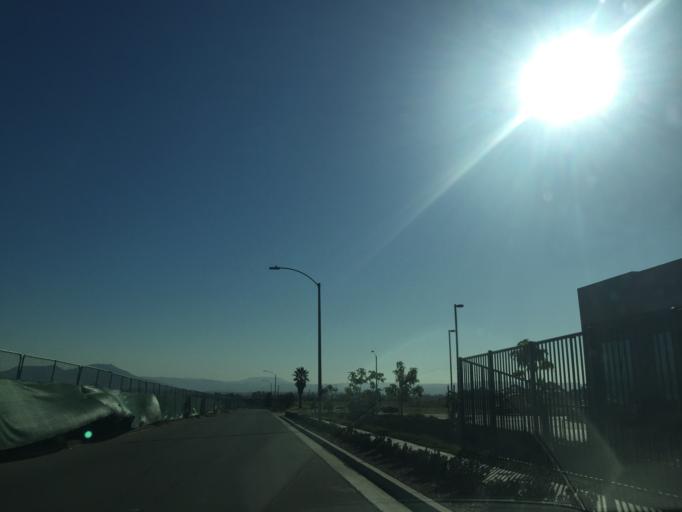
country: MX
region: Baja California
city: Tijuana
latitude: 32.5594
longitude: -116.9234
